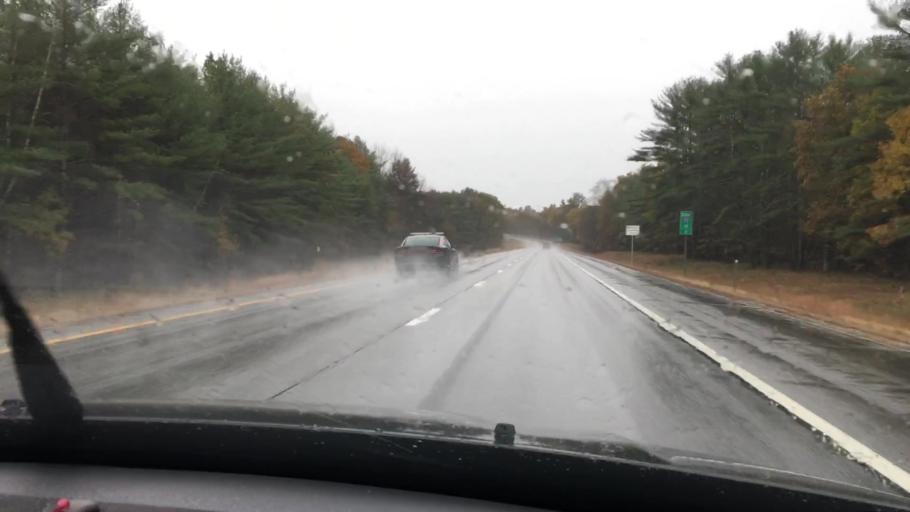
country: US
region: New Hampshire
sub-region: Merrimack County
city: East Concord
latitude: 43.2789
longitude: -71.5659
